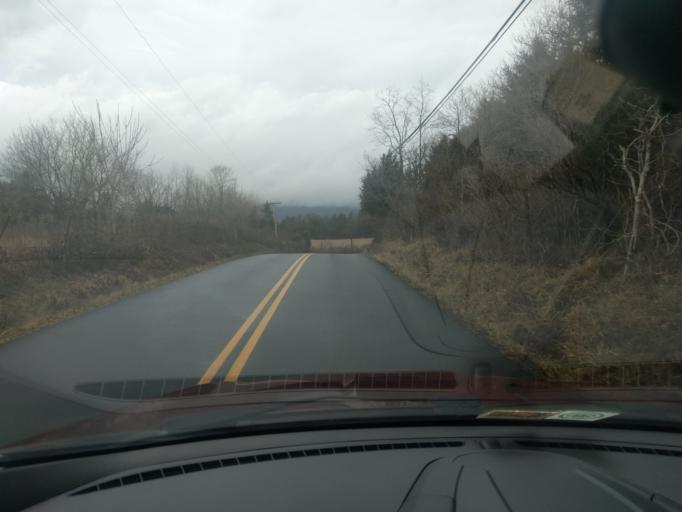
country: US
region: Virginia
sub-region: Botetourt County
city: Fincastle
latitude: 37.5231
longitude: -79.8814
